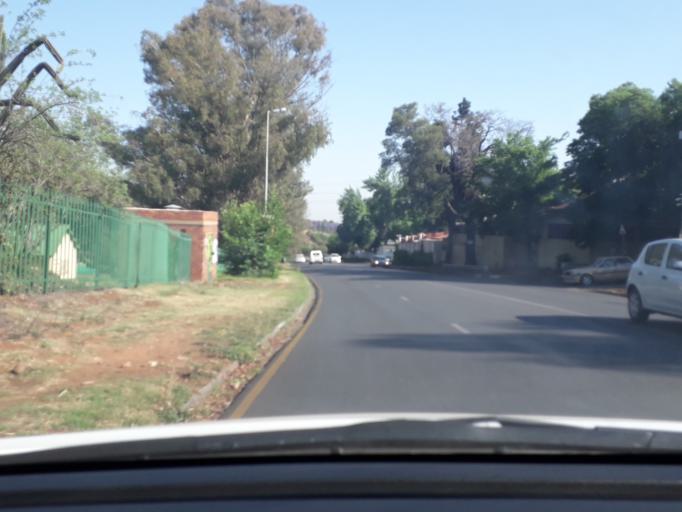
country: ZA
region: Gauteng
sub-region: City of Johannesburg Metropolitan Municipality
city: Johannesburg
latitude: -26.1735
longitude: 28.0003
